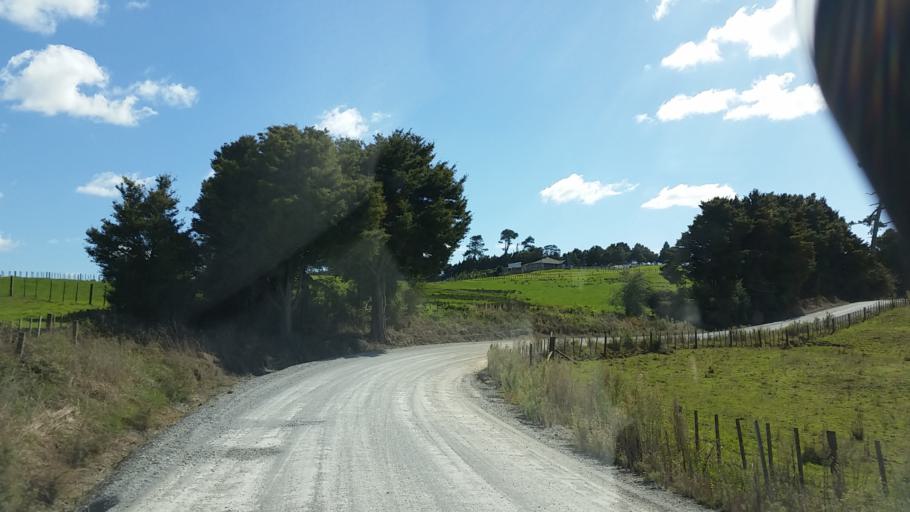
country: NZ
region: Northland
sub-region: Whangarei
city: Maungatapere
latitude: -35.6924
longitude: 174.2172
